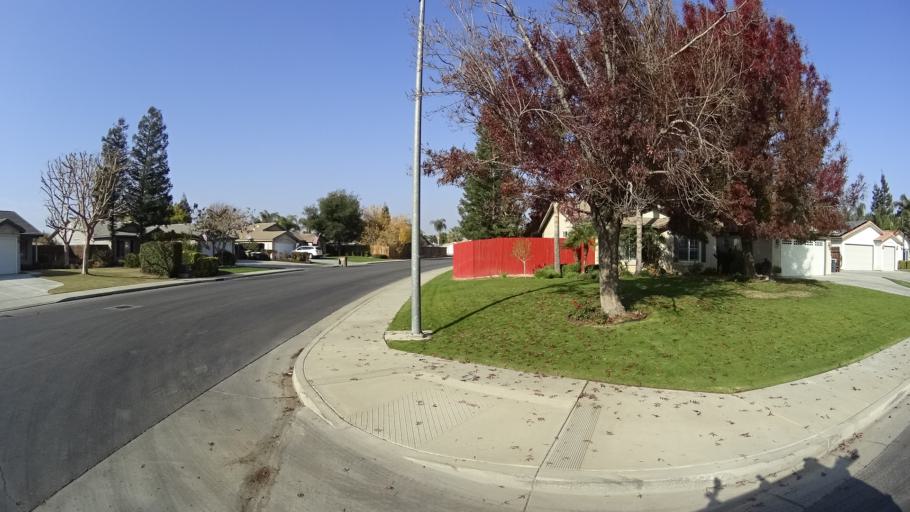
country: US
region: California
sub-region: Kern County
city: Oildale
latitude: 35.4041
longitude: -119.0628
